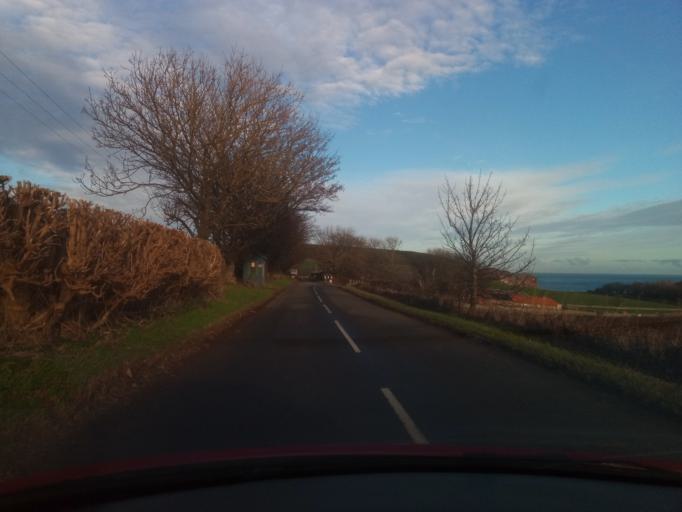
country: GB
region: Scotland
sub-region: The Scottish Borders
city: Eyemouth
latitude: 55.8984
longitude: -2.1416
